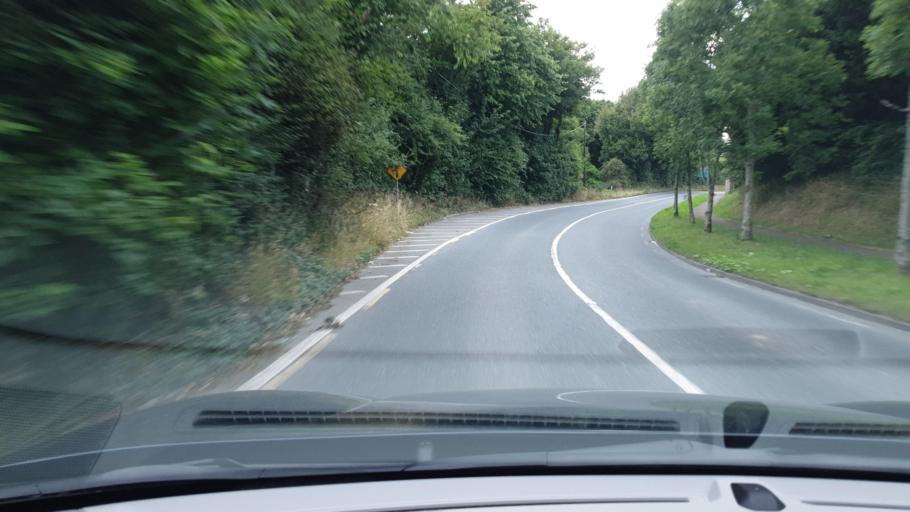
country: IE
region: Leinster
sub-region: South Dublin
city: Saggart
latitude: 53.2748
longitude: -6.4416
